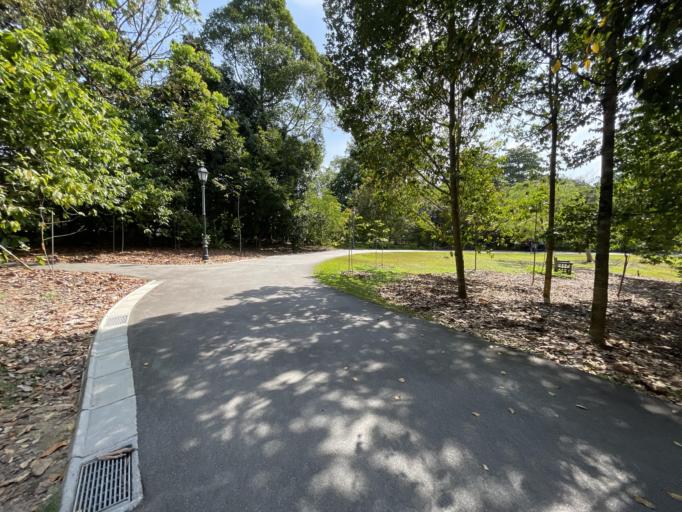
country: SG
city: Singapore
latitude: 1.3216
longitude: 103.8171
